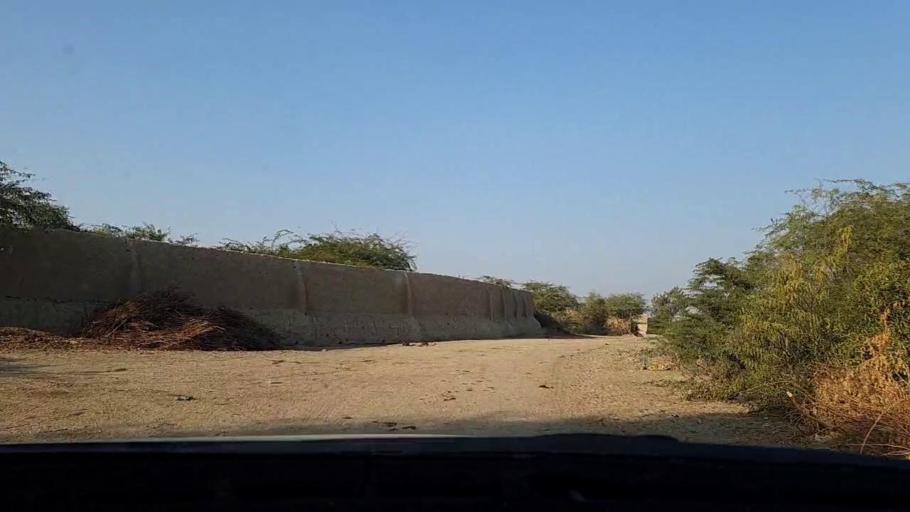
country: PK
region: Sindh
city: Tando Mittha Khan
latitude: 25.8597
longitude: 69.3167
